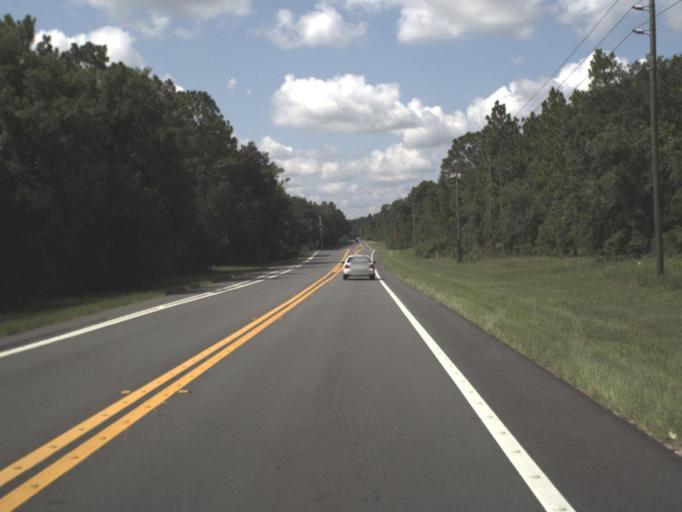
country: US
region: Florida
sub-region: Citrus County
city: Floral City
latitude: 28.6865
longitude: -82.3202
